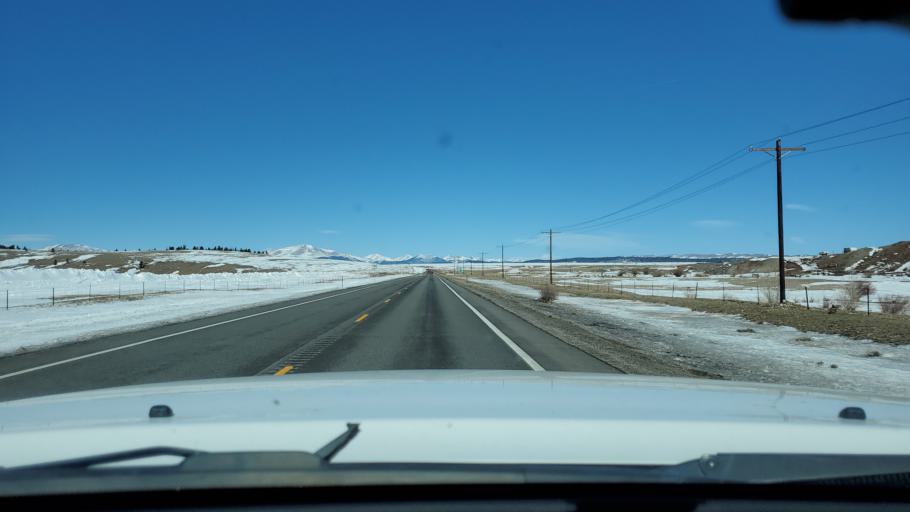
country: US
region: Colorado
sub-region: Park County
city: Fairplay
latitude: 39.0655
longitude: -105.9742
